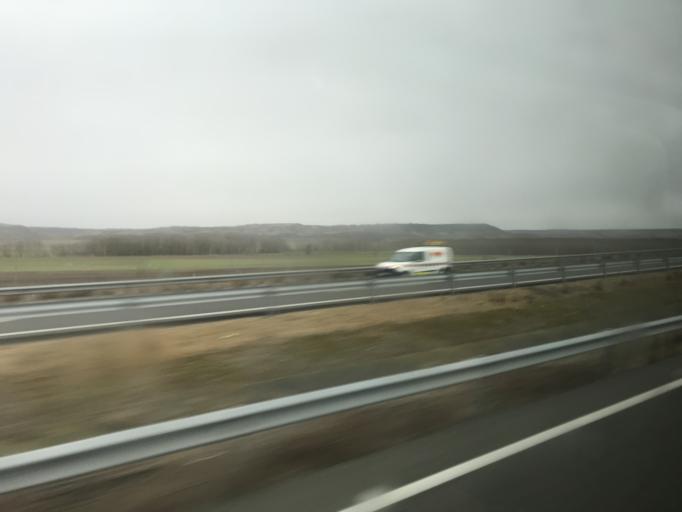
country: ES
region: Castille and Leon
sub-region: Provincia de Burgos
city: Villaverde-Mogina
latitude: 42.1671
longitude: -4.0734
